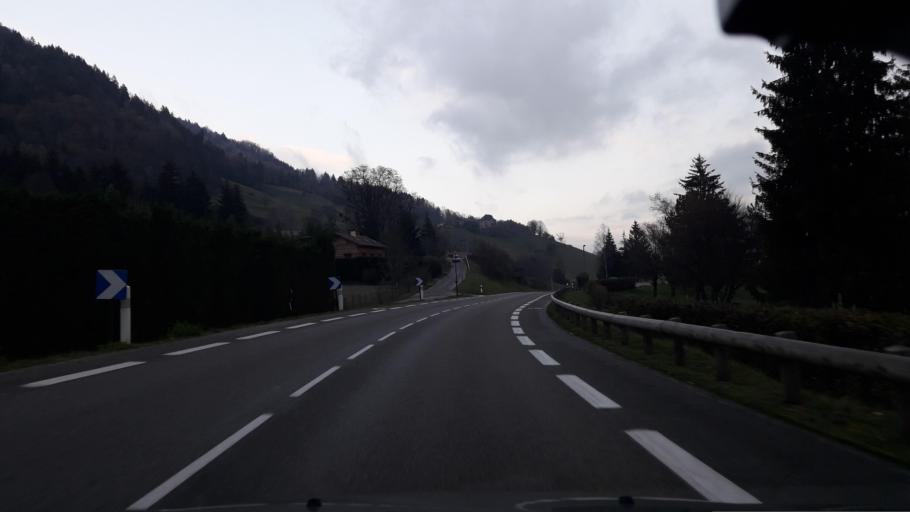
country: FR
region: Rhone-Alpes
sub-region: Departement de l'Isere
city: Allevard
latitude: 45.3811
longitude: 6.0536
